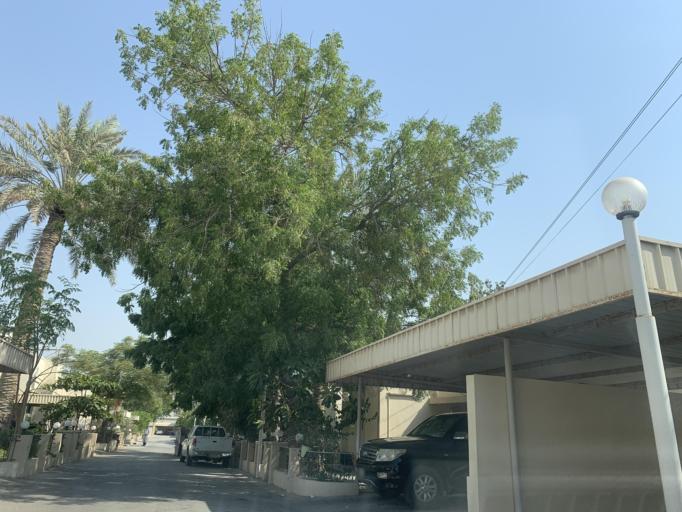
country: BH
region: Manama
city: Jidd Hafs
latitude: 26.2042
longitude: 50.5287
